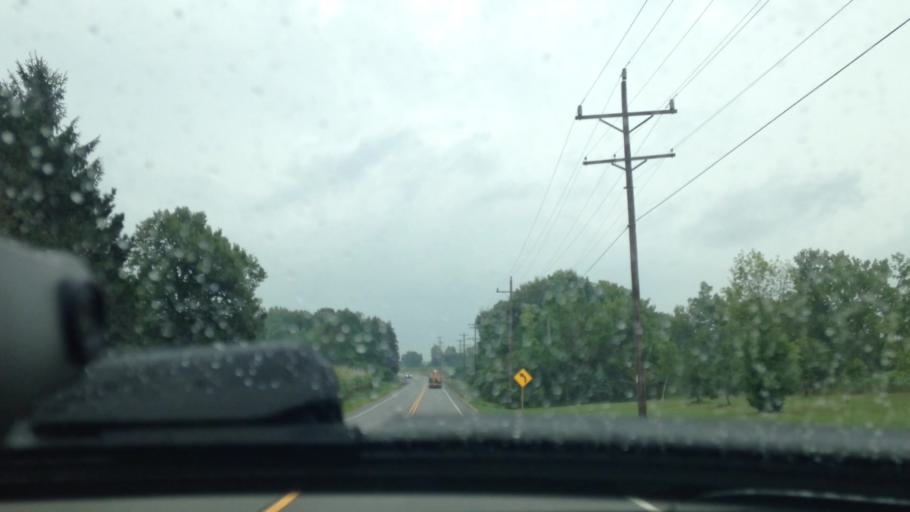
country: US
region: Wisconsin
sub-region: Washington County
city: Slinger
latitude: 43.3178
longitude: -88.2661
